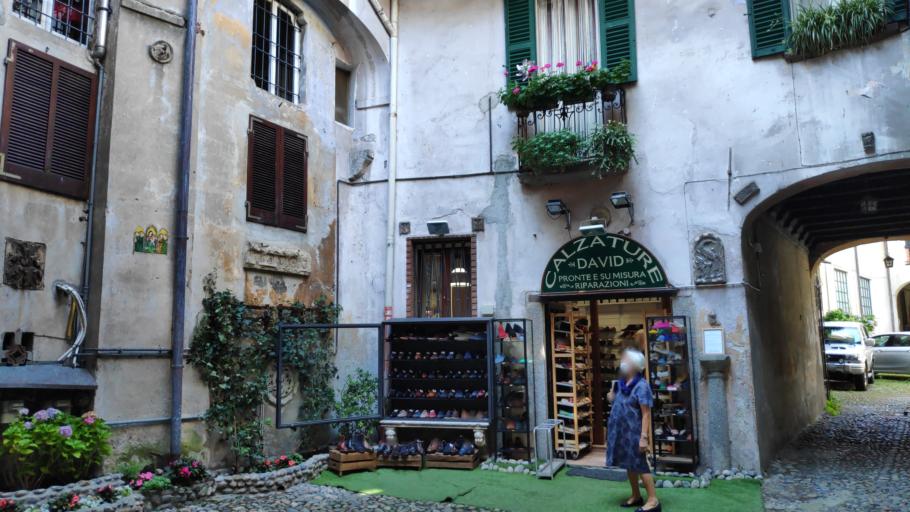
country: IT
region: Piedmont
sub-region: Provincia di Novara
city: Arona
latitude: 45.7619
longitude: 8.5607
